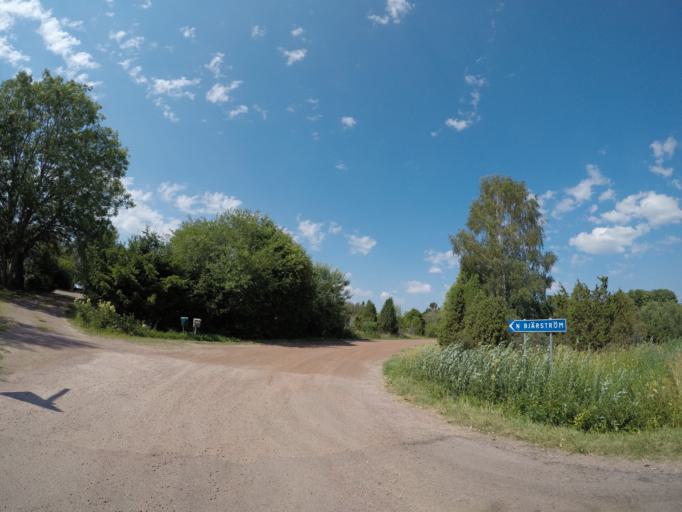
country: AX
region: Alands landsbygd
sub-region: Finstroem
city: Finstroem
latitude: 60.2136
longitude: 19.8572
